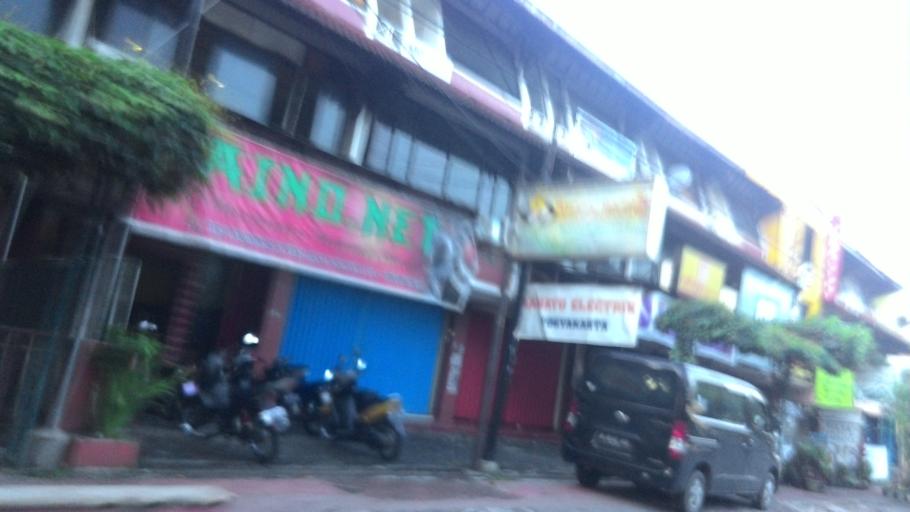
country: ID
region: Daerah Istimewa Yogyakarta
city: Yogyakarta
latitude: -7.7831
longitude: 110.3847
